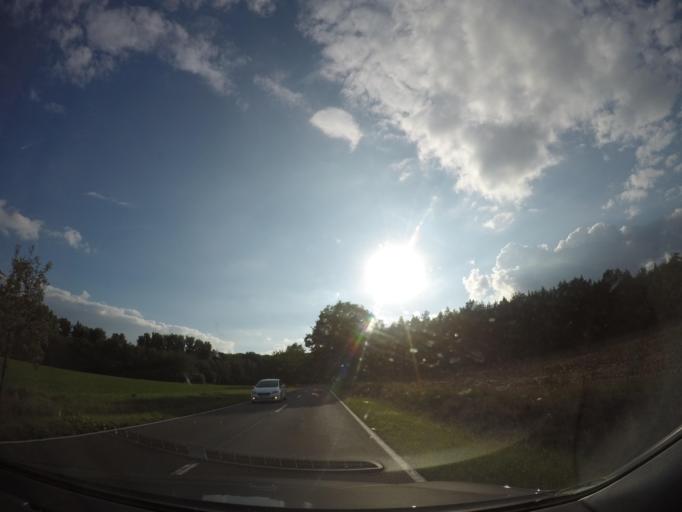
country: DE
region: Saxony-Anhalt
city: Weferlingen
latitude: 52.3650
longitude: 11.0899
